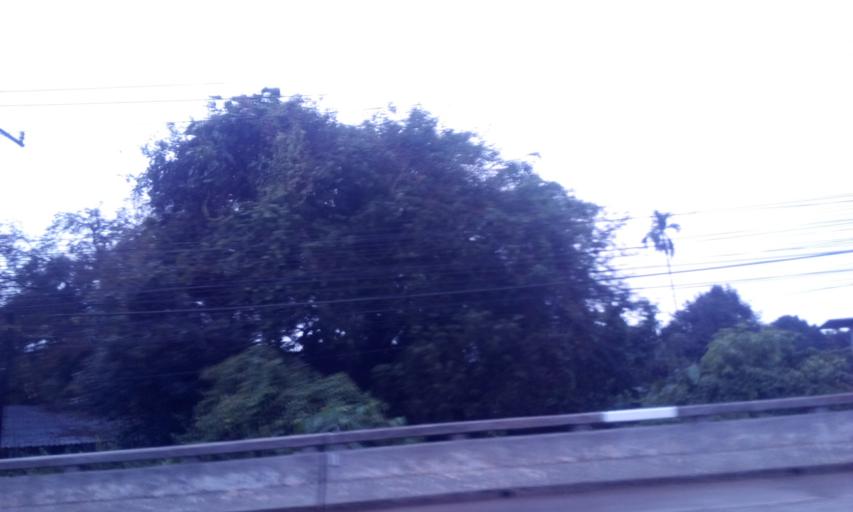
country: TH
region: Trat
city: Khao Saming
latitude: 12.3742
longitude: 102.3839
